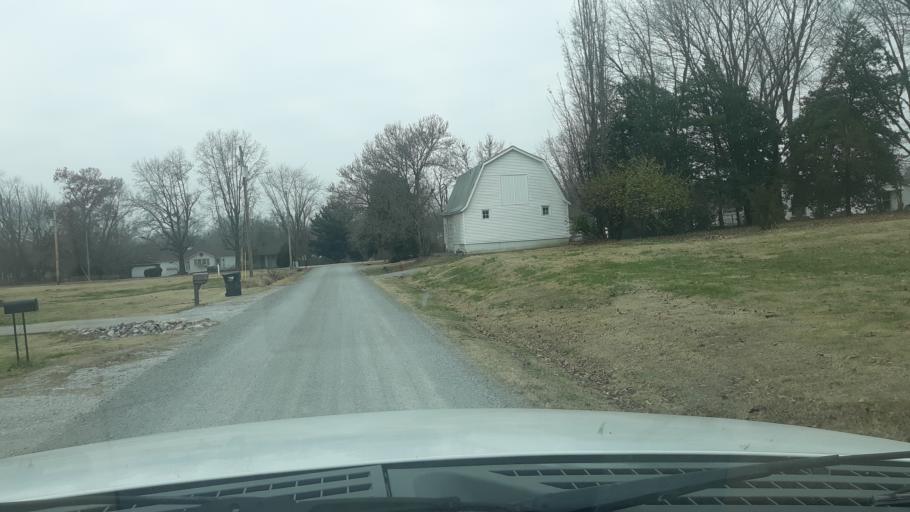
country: US
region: Illinois
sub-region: Saline County
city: Harrisburg
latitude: 37.8376
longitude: -88.6107
